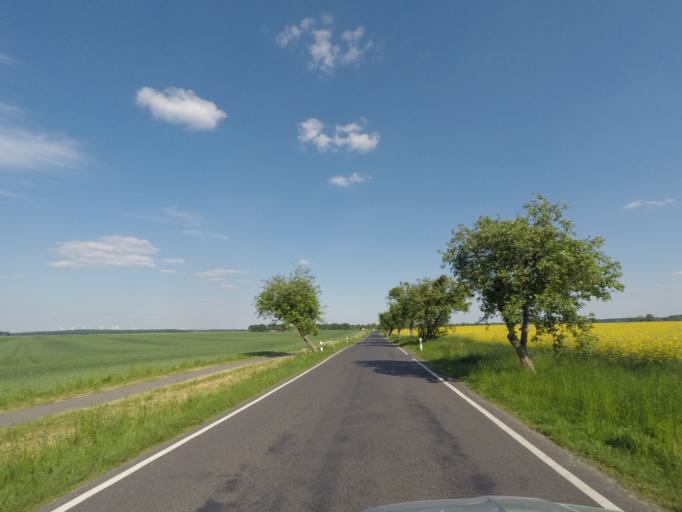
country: DE
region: Brandenburg
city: Werftpfuhl
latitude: 52.7334
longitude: 13.8569
